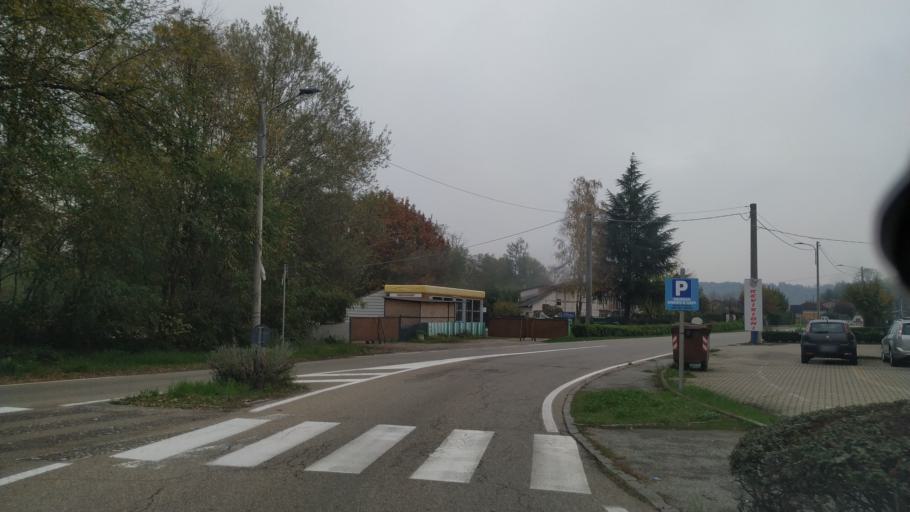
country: IT
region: Piedmont
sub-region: Provincia di Biella
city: Cerreto Castello
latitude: 45.5587
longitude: 8.1714
